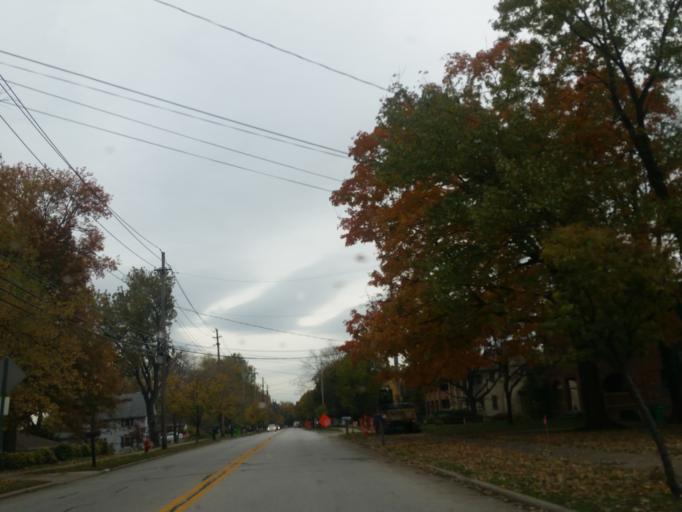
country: US
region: Ohio
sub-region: Cuyahoga County
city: Brooklyn Heights
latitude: 41.4195
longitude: -81.6738
